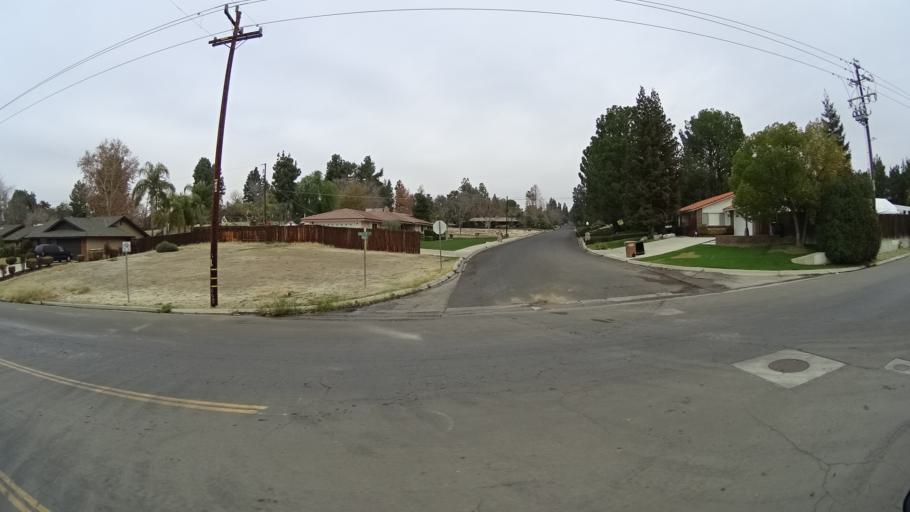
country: US
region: California
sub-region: Kern County
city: Bakersfield
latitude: 35.3831
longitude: -118.9443
